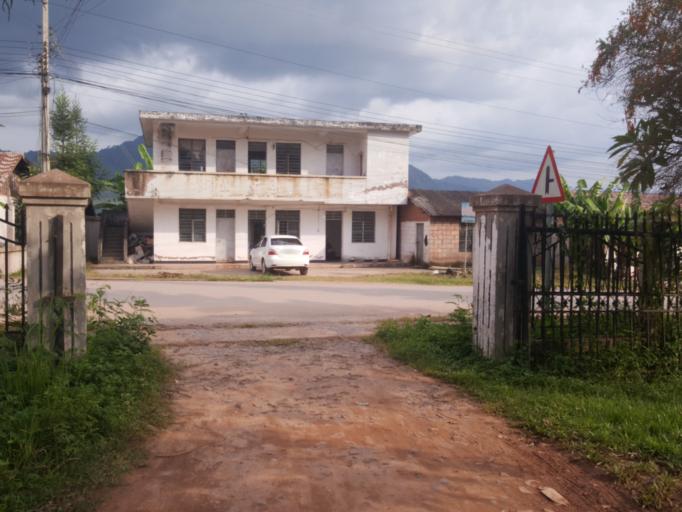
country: CN
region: Yunnan
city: Menglie
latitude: 22.1239
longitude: 101.7876
